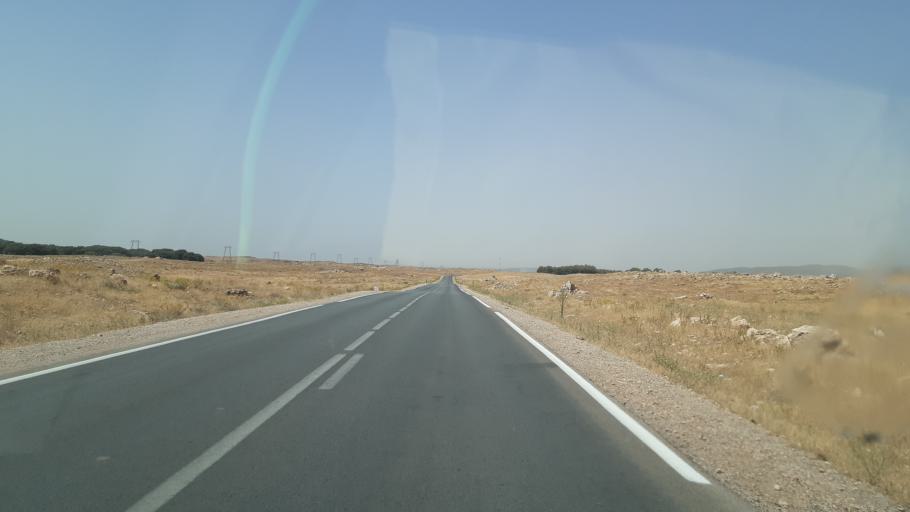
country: MA
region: Meknes-Tafilalet
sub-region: Ifrane
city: Ifrane
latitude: 33.5639
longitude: -5.0964
